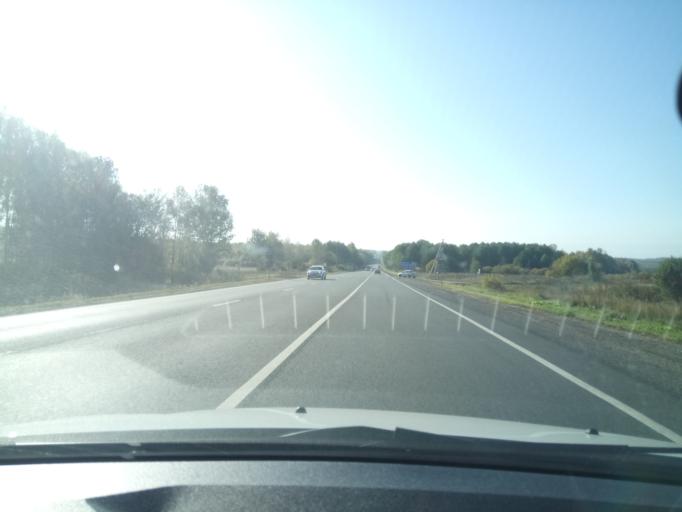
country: RU
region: Nizjnij Novgorod
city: Dal'neye Konstantinovo
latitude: 55.9893
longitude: 43.9695
